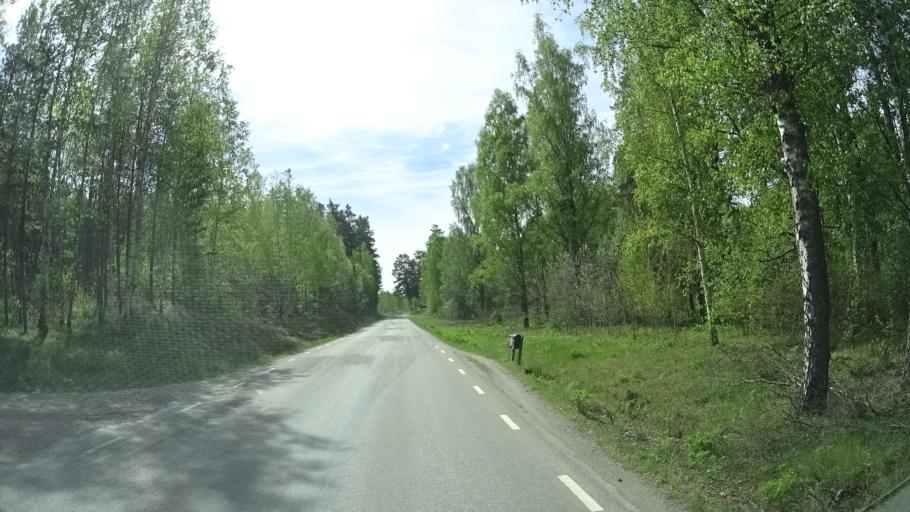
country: SE
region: OEstergoetland
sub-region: Finspangs Kommun
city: Finspang
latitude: 58.7476
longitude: 15.8284
